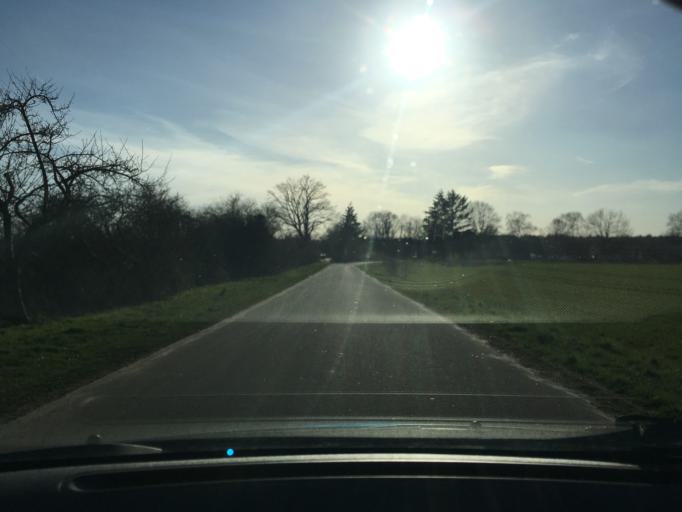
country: DE
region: Lower Saxony
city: Embsen
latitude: 53.2142
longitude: 10.3637
